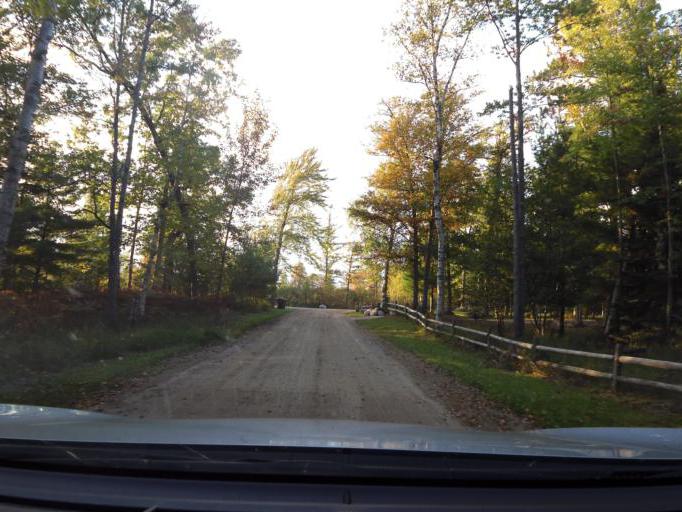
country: US
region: Michigan
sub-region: Roscommon County
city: Saint Helen
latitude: 44.3591
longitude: -84.4709
